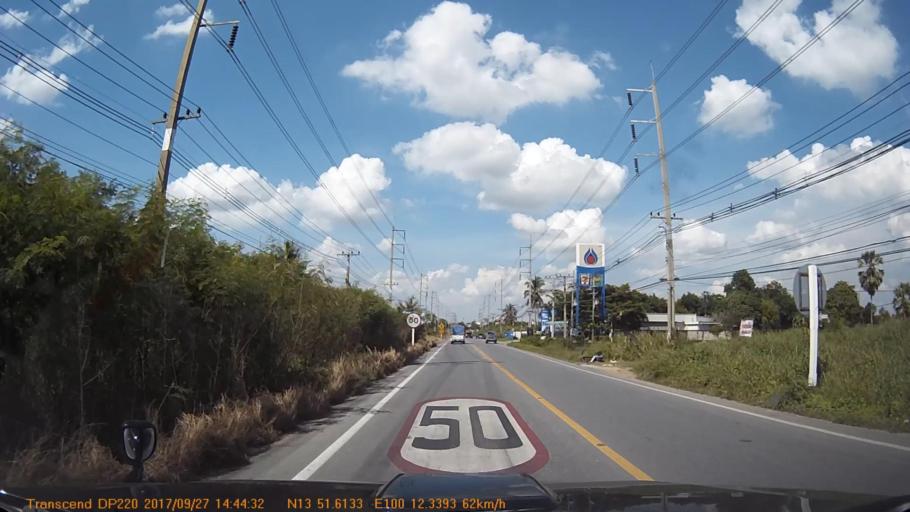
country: TH
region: Nakhon Pathom
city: Nakhon Chai Si
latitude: 13.8603
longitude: 100.2057
